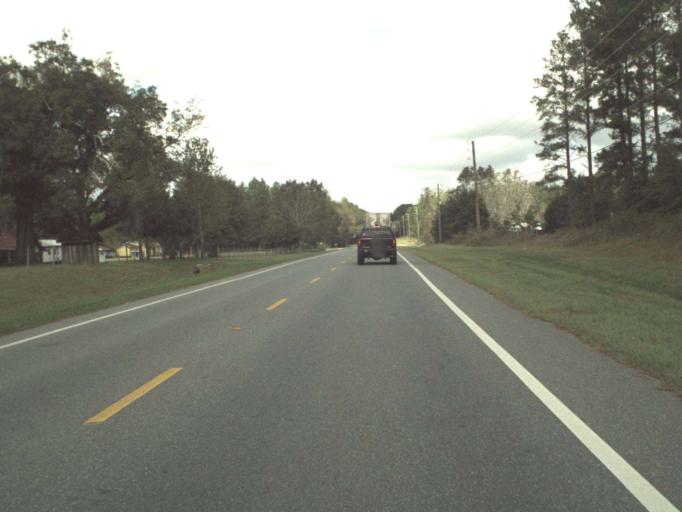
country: US
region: Florida
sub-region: Jackson County
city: Malone
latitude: 30.9108
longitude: -85.1608
